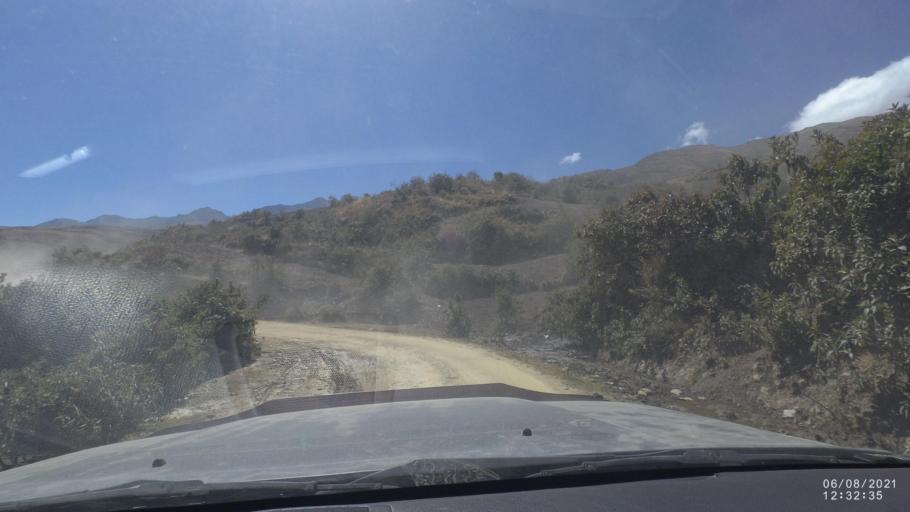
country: BO
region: Cochabamba
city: Colchani
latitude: -16.7832
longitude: -66.6458
